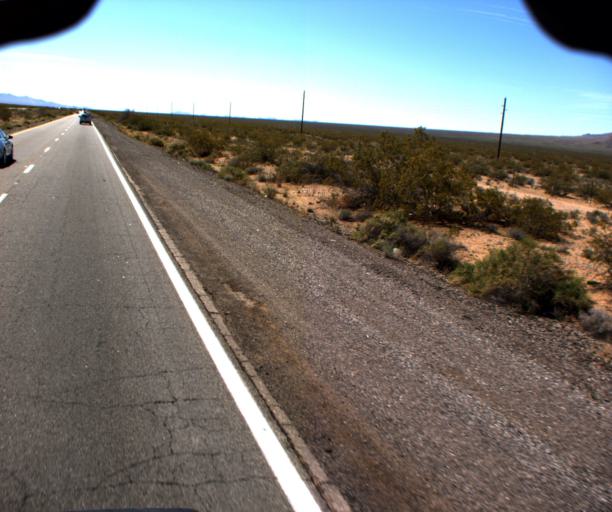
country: US
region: Arizona
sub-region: Mohave County
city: Dolan Springs
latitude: 35.6540
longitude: -114.4445
